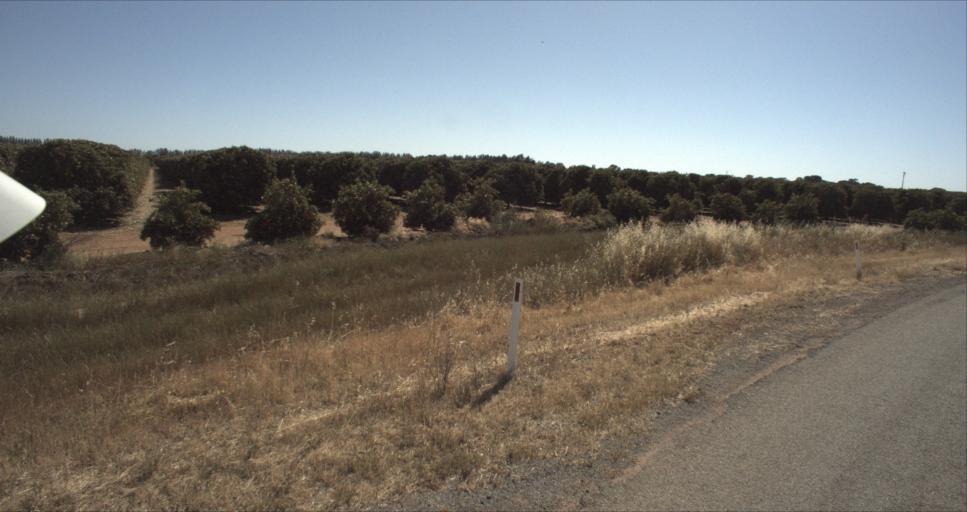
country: AU
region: New South Wales
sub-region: Leeton
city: Leeton
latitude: -34.5336
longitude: 146.3254
